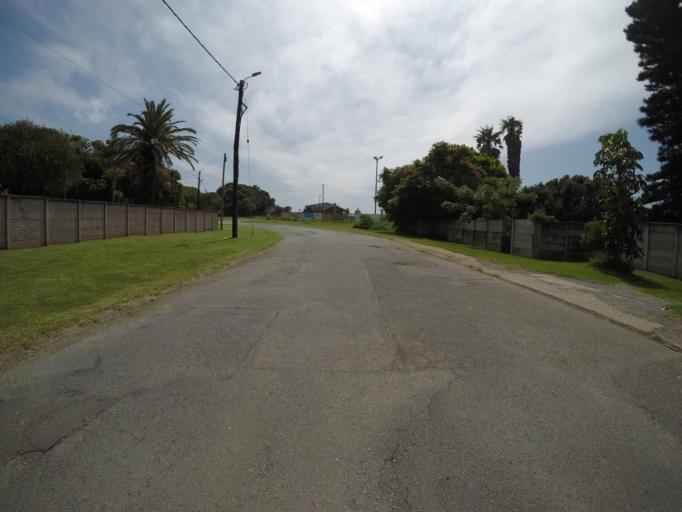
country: ZA
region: Eastern Cape
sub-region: Buffalo City Metropolitan Municipality
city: East London
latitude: -32.9392
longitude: 28.0234
